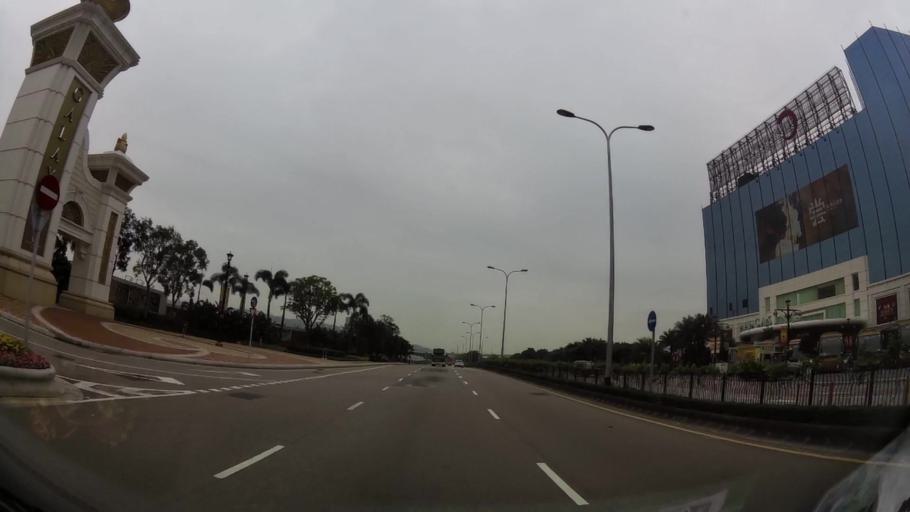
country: MO
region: Macau
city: Macau
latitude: 22.1460
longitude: 113.5528
